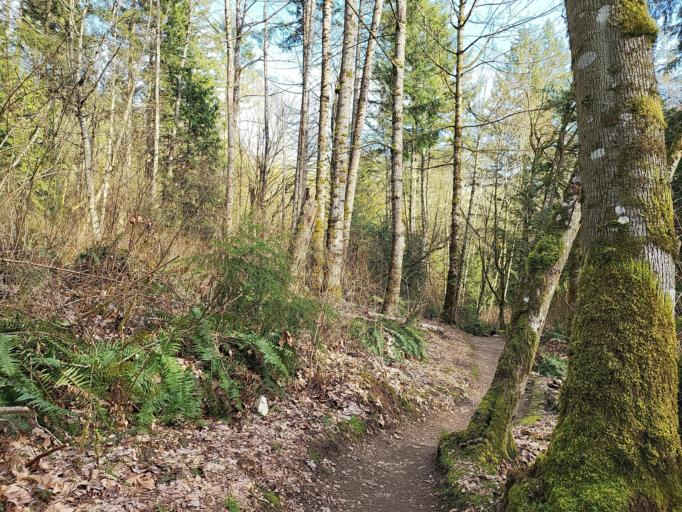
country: US
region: Washington
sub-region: King County
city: East Renton Highlands
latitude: 47.5170
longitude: -122.1243
